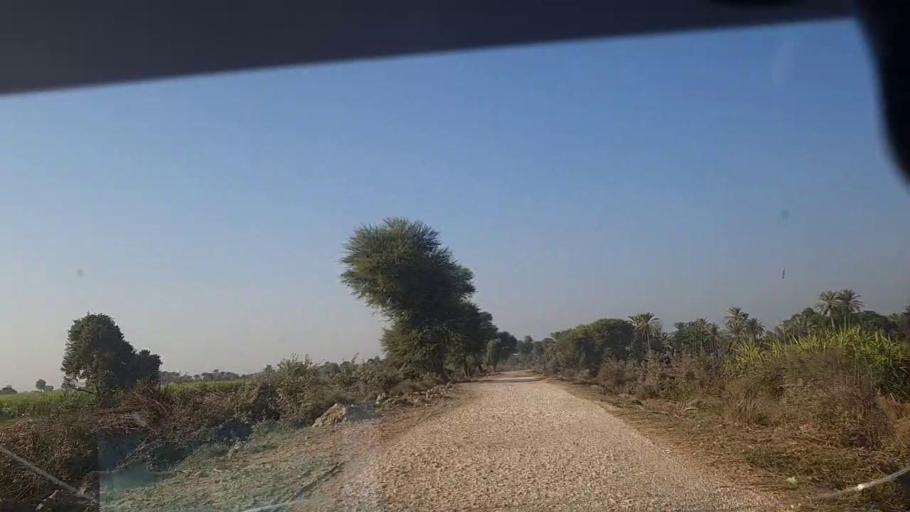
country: PK
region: Sindh
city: Sobhadero
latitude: 27.2655
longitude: 68.3491
